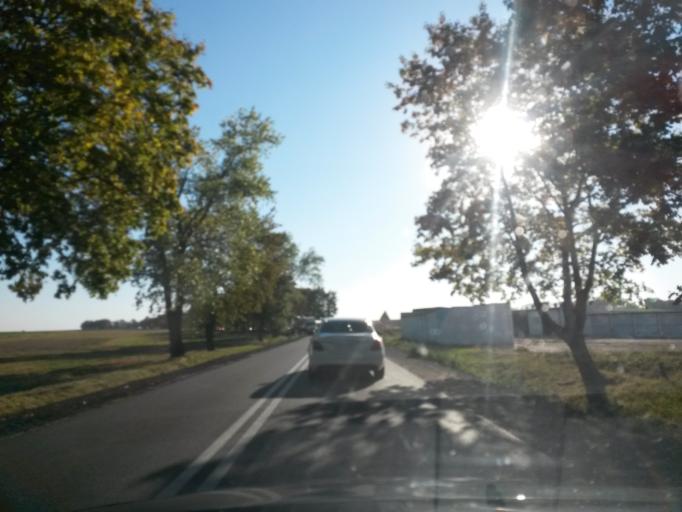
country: PL
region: Lower Silesian Voivodeship
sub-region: Powiat sredzki
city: Udanin
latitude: 51.0806
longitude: 16.4137
